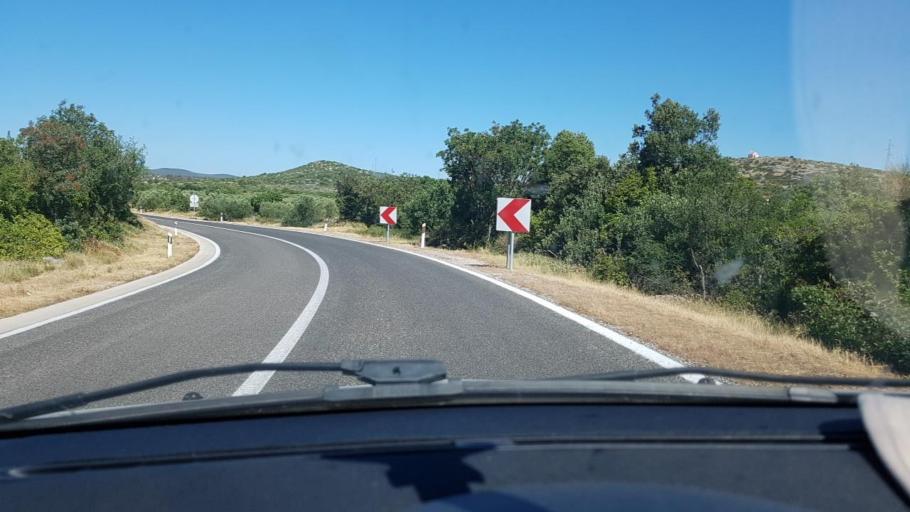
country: HR
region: Sibensko-Kniniska
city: Zaton
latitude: 43.7619
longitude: 15.8375
